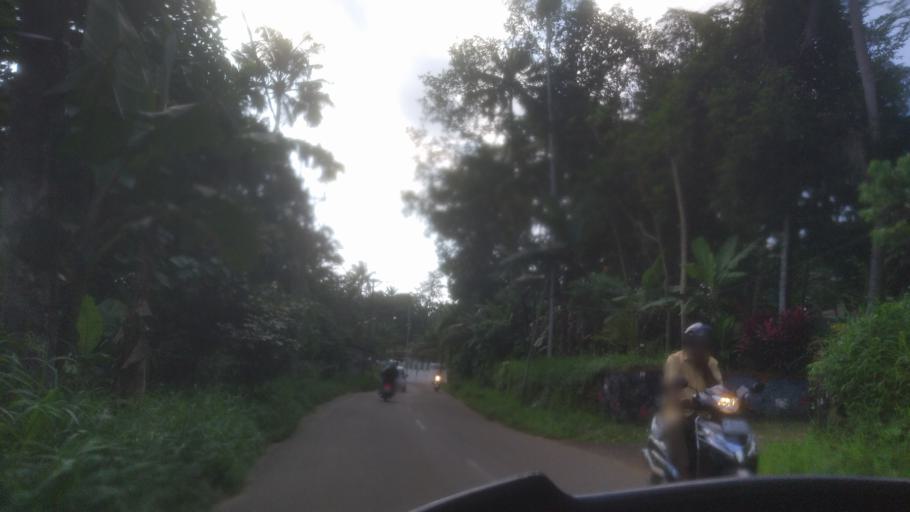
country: IN
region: Kerala
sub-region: Ernakulam
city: Muvattupula
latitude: 9.9961
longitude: 76.6084
